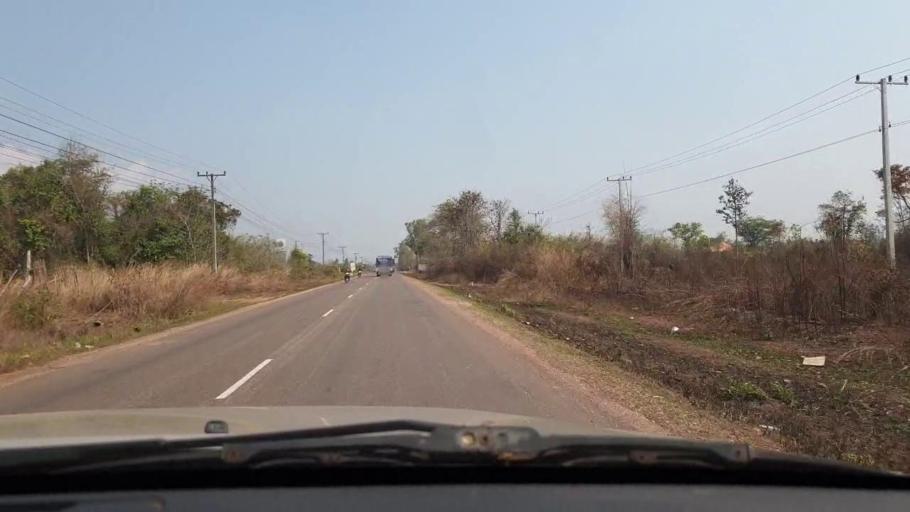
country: TH
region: Nong Khai
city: Phon Phisai
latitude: 18.1124
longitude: 103.0263
